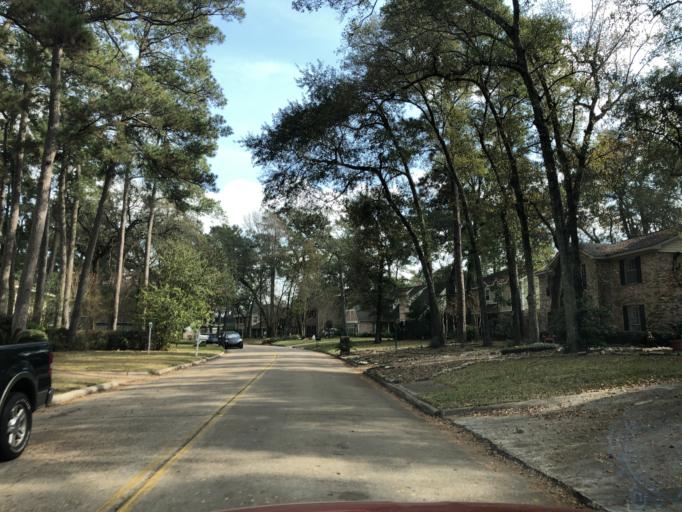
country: US
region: Texas
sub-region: Harris County
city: Tomball
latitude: 30.0291
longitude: -95.5371
